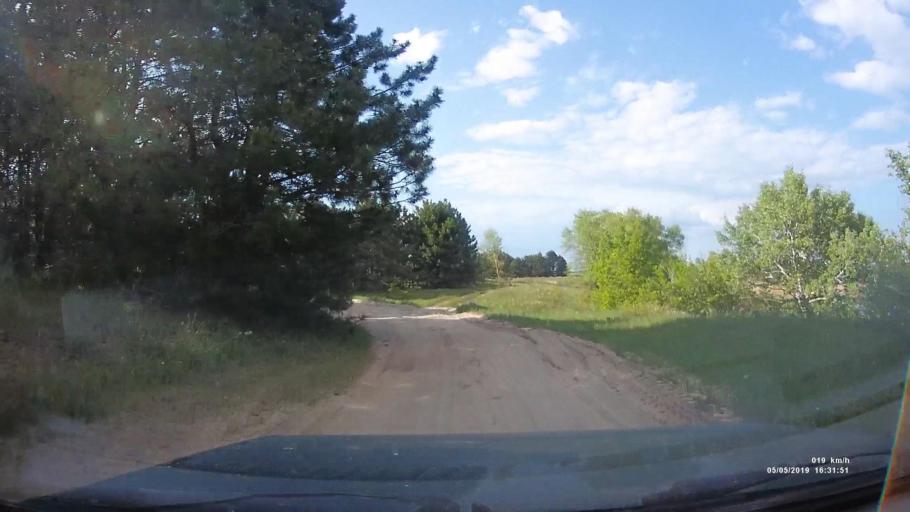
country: RU
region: Rostov
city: Ust'-Donetskiy
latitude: 47.7773
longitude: 41.0143
